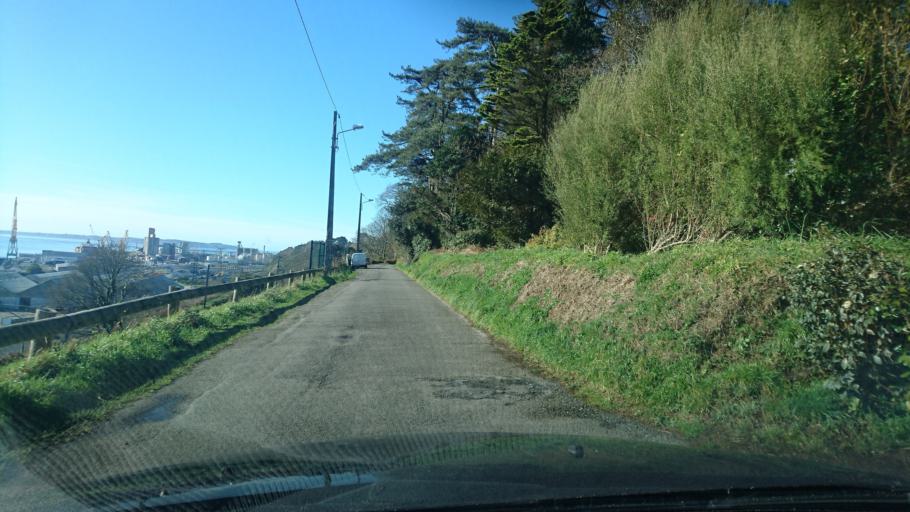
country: FR
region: Brittany
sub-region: Departement du Finistere
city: Brest
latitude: 48.3938
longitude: -4.4517
